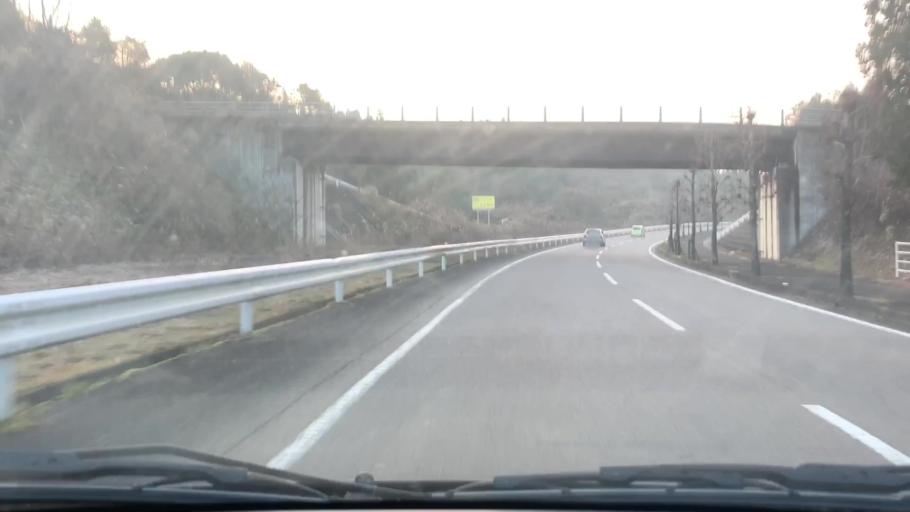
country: JP
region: Saga Prefecture
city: Imaricho-ko
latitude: 33.2592
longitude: 129.9253
